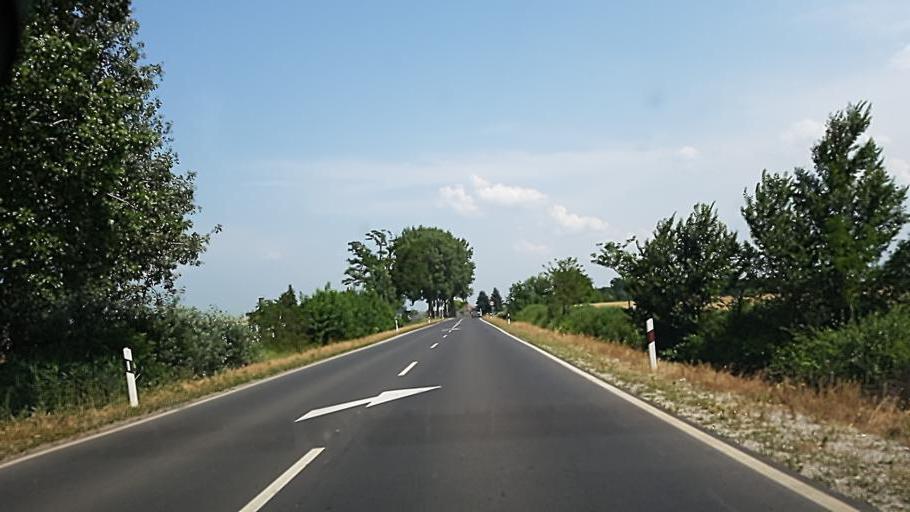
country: HU
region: Heves
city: Poroszlo
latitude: 47.6472
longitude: 20.6297
